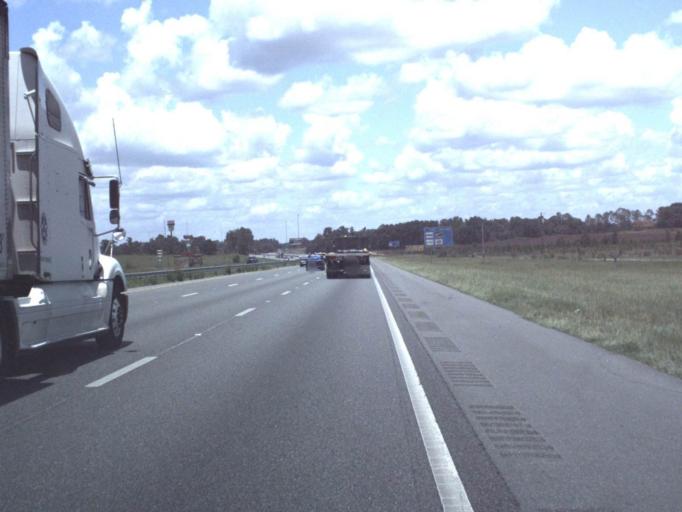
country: US
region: Florida
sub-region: Hamilton County
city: Jasper
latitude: 30.5091
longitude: -83.0488
